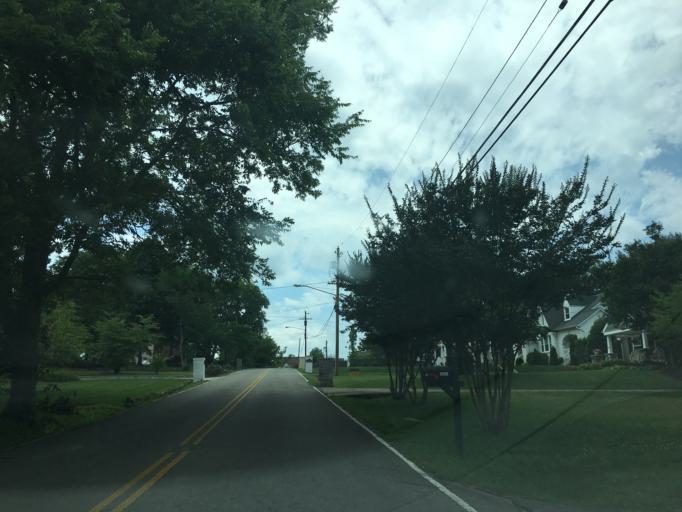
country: US
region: Tennessee
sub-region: Davidson County
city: Oak Hill
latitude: 36.1006
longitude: -86.8073
